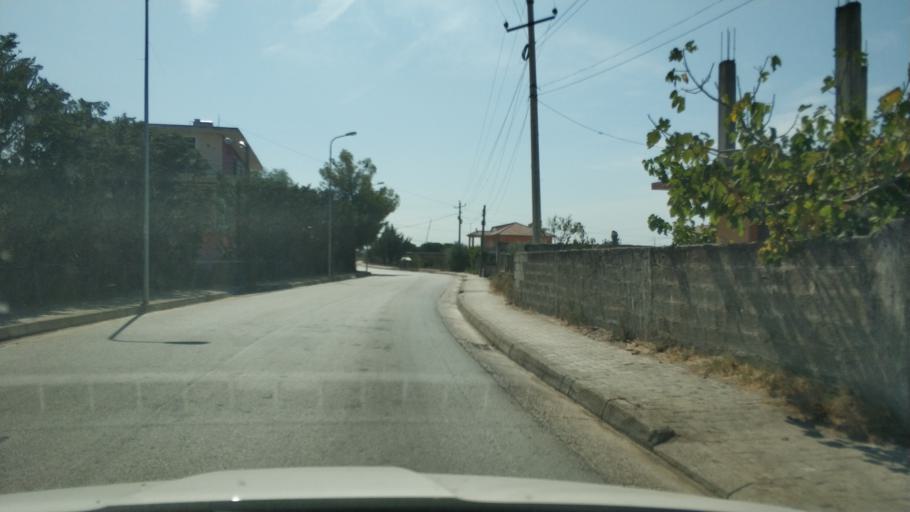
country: AL
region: Fier
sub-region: Rrethi i Lushnjes
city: Divjake
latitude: 40.9883
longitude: 19.5344
